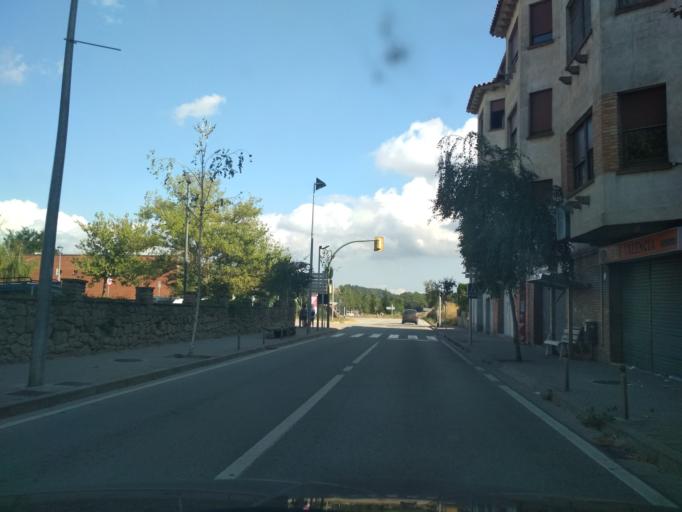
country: ES
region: Catalonia
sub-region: Provincia de Barcelona
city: Castelltercol
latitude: 41.7499
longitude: 2.1237
